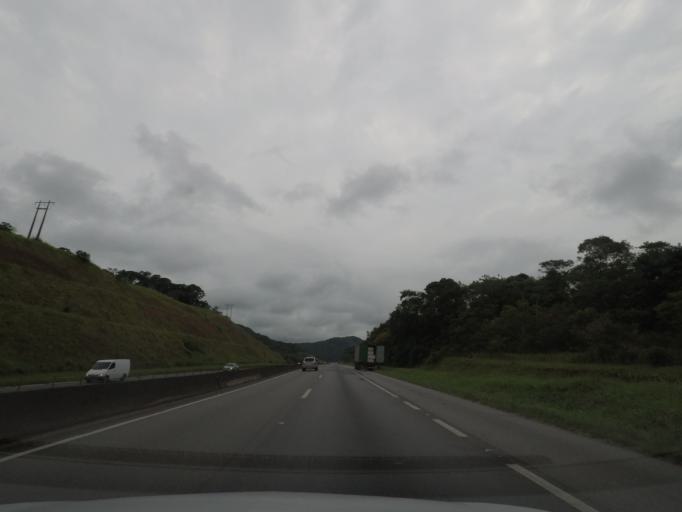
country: BR
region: Sao Paulo
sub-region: Juquia
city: Juquia
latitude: -24.3494
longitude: -47.6527
